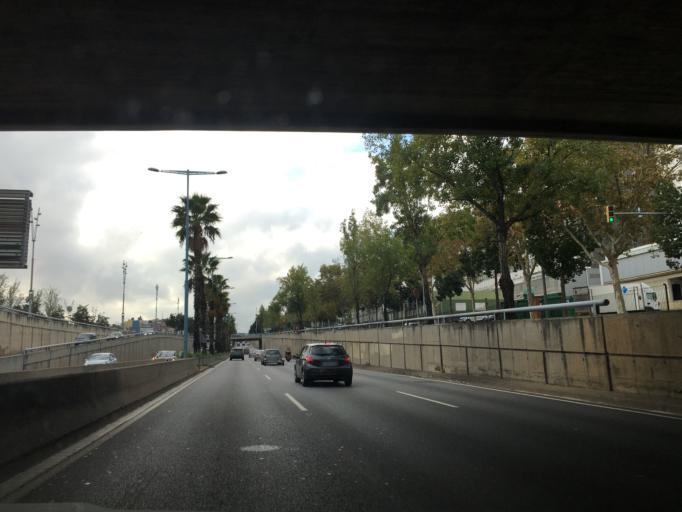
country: ES
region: Catalonia
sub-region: Provincia de Barcelona
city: Horta-Guinardo
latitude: 41.4298
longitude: 2.1446
